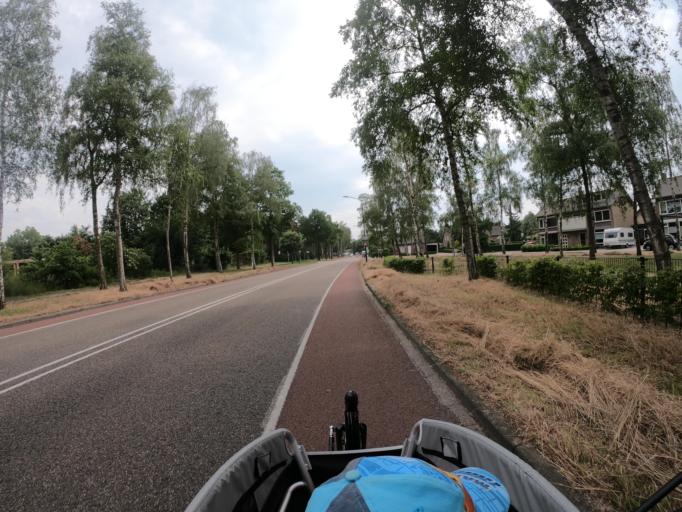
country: NL
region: North Brabant
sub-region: Gemeente Uden
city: Uden
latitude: 51.6582
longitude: 5.6290
